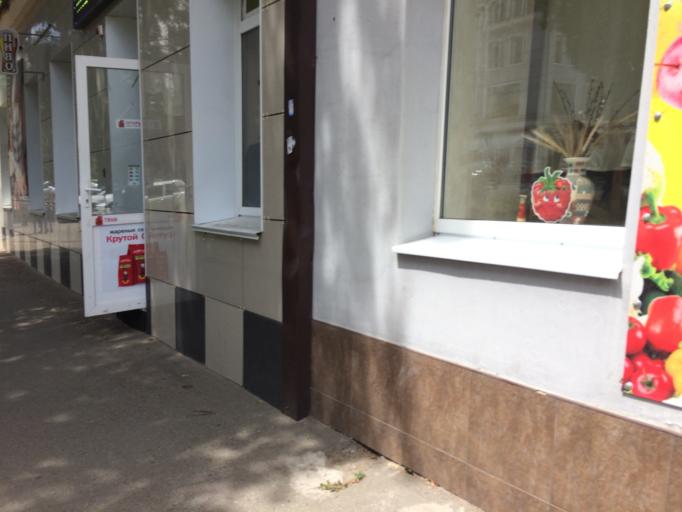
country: RU
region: Stavropol'skiy
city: Stavropol'
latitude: 45.0426
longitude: 41.9552
